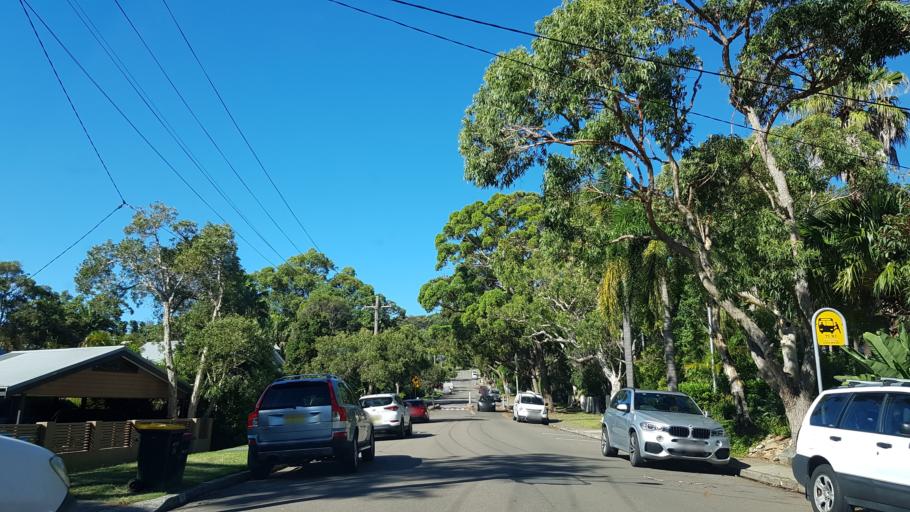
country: AU
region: New South Wales
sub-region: Pittwater
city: Bilgola Beach
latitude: -33.6241
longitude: 151.3352
